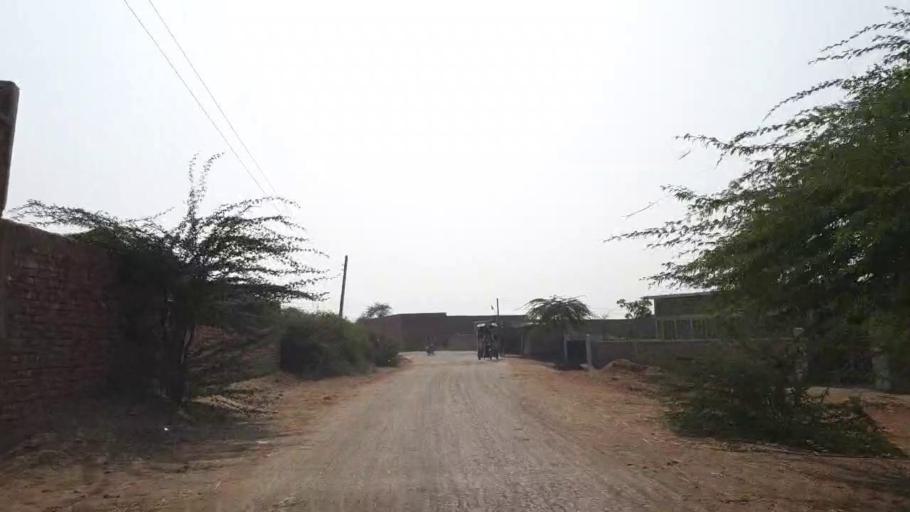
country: PK
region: Sindh
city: Matli
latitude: 24.9637
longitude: 68.5841
